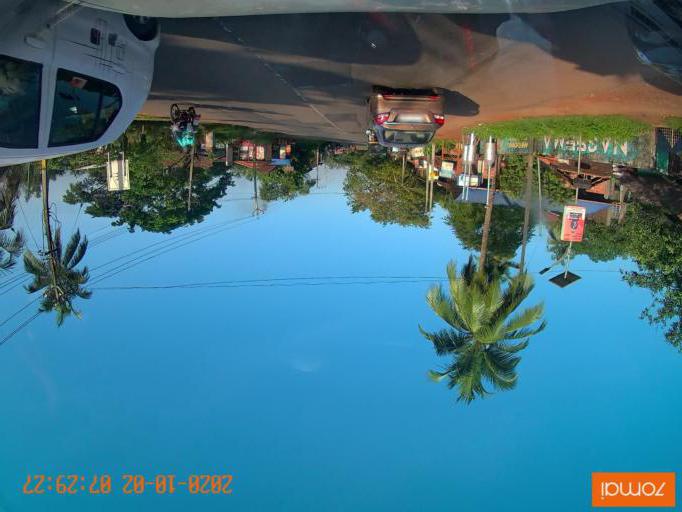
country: IN
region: Kerala
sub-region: Malappuram
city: Pariyapuram
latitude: 11.0345
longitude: 75.9389
